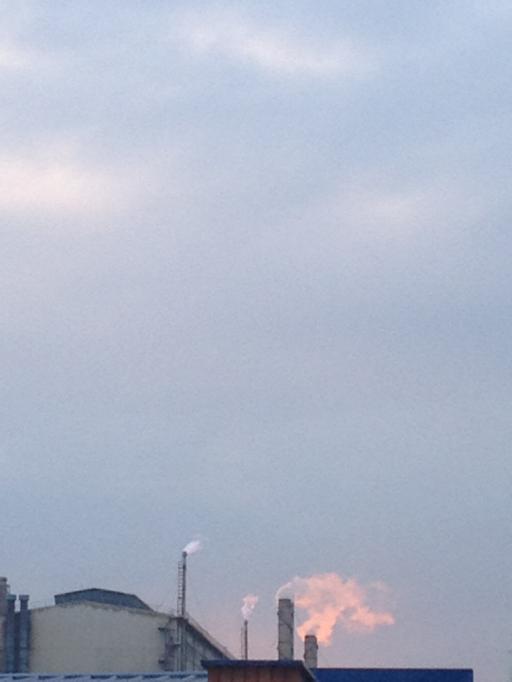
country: XK
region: Pristina
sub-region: Komuna e Drenasit
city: Glogovac
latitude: 42.6418
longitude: 20.9052
